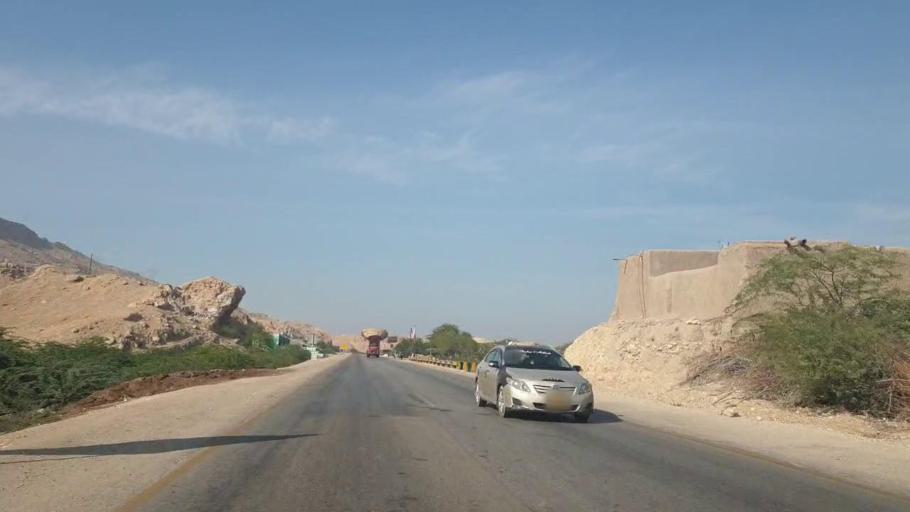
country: PK
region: Sindh
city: Sehwan
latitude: 26.3015
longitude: 67.8946
